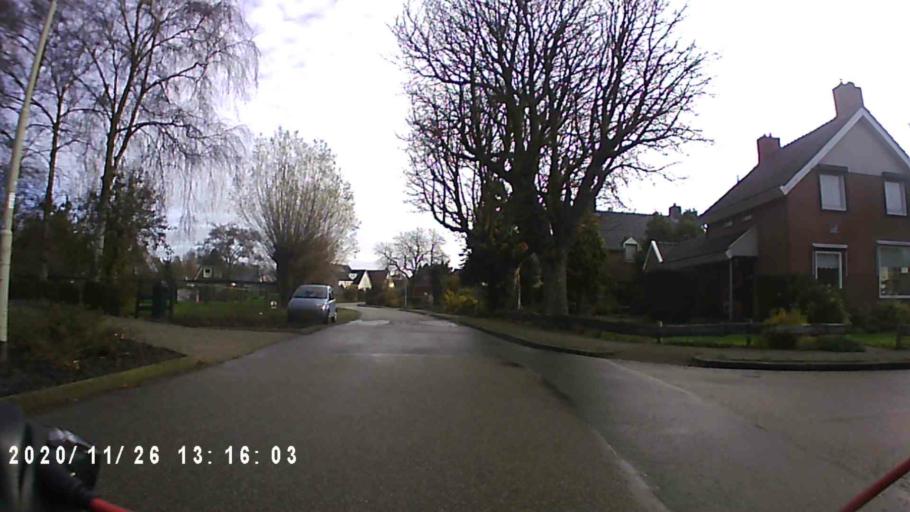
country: NL
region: Groningen
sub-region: Gemeente Appingedam
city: Appingedam
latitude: 53.3581
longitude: 6.8753
